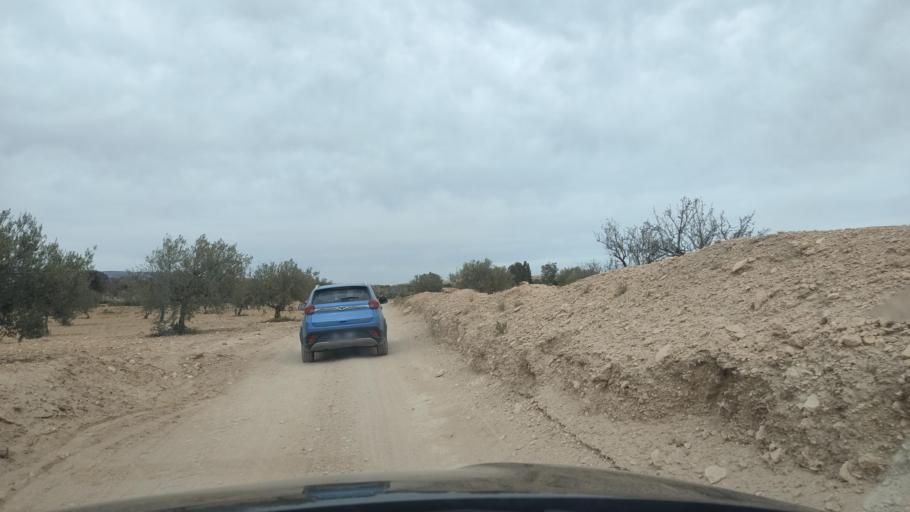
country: TN
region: Al Qasrayn
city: Kasserine
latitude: 35.2549
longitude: 8.9216
